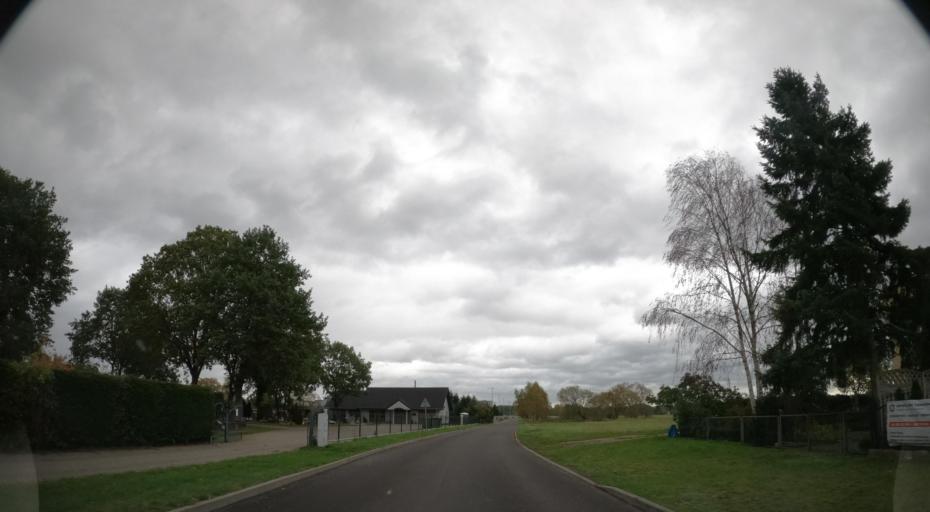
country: PL
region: West Pomeranian Voivodeship
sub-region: Powiat goleniowski
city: Stepnica
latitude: 53.6506
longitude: 14.6324
